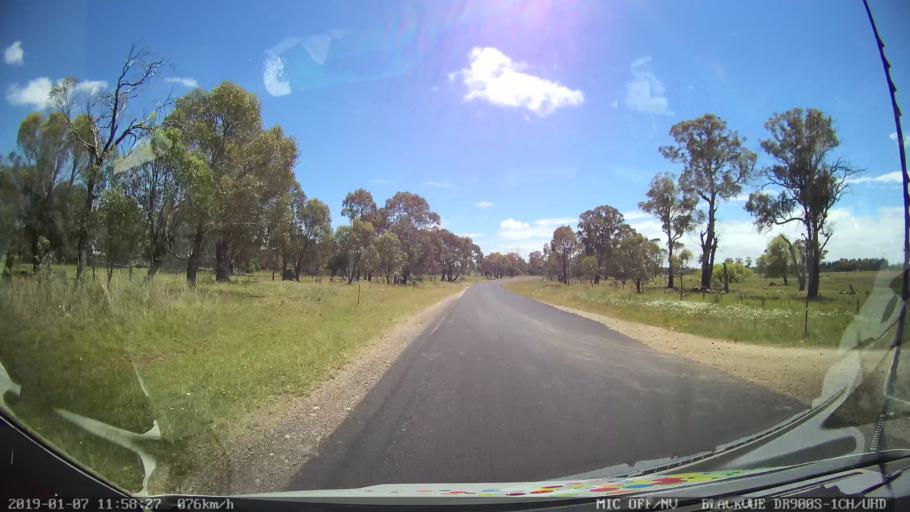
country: AU
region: New South Wales
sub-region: Guyra
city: Guyra
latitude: -30.2531
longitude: 151.6674
